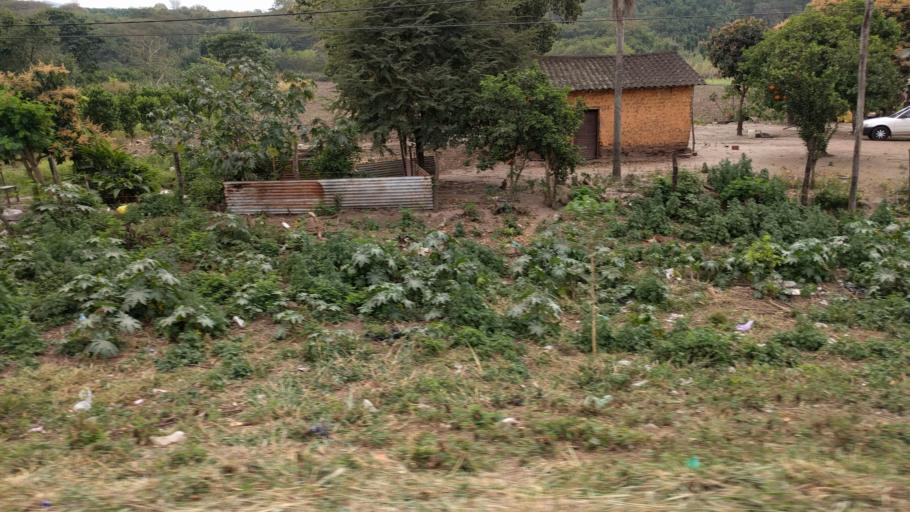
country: BO
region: Santa Cruz
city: Jorochito
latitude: -18.1548
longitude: -63.4965
